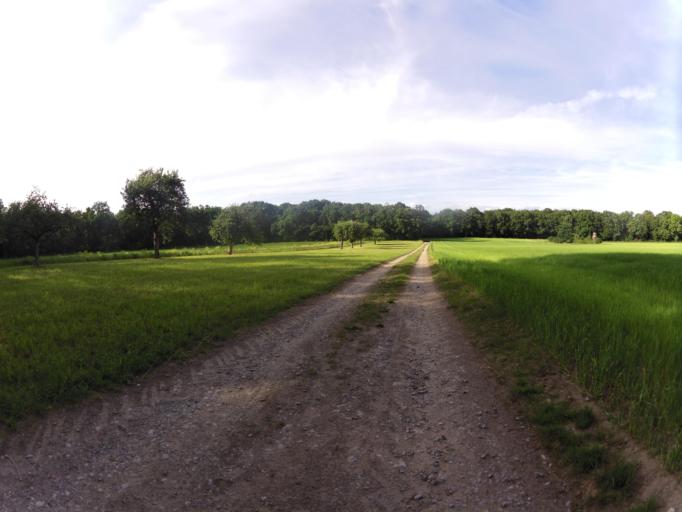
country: DE
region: Bavaria
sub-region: Regierungsbezirk Unterfranken
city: Frickenhausen
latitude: 49.6926
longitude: 10.0738
